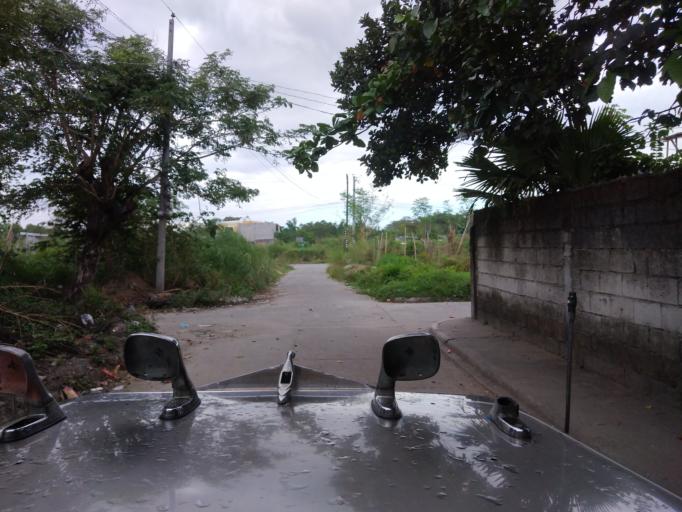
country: PH
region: Central Luzon
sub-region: Province of Pampanga
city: Pandacaqui
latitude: 15.1858
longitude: 120.6484
